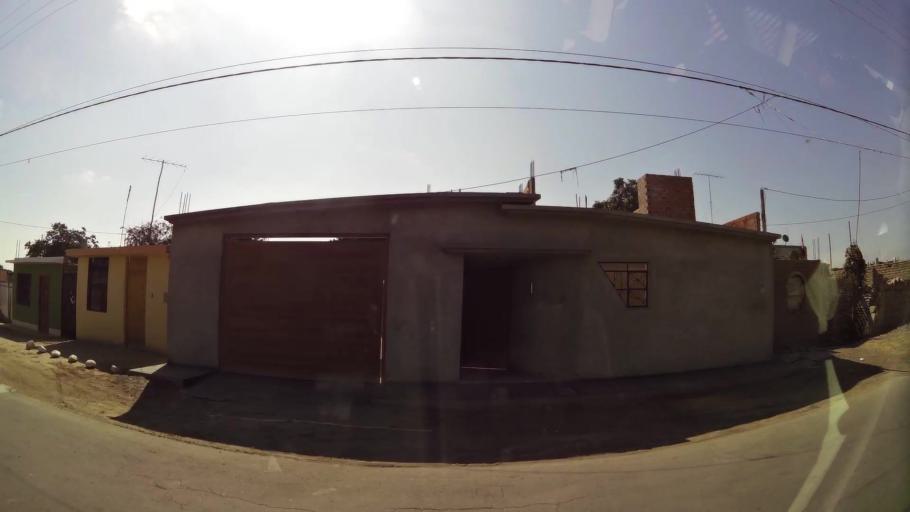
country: PE
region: Ica
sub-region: Provincia de Chincha
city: Sunampe
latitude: -13.4189
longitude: -76.1614
